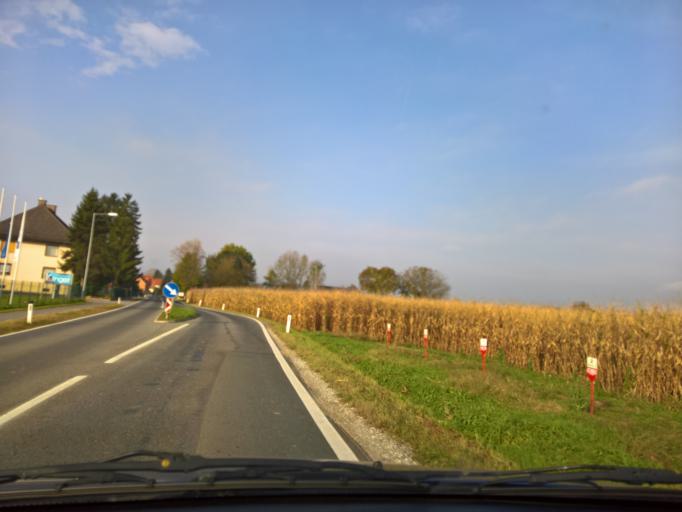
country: AT
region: Styria
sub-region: Politischer Bezirk Deutschlandsberg
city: Gross Sankt Florian
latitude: 46.8226
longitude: 15.2902
